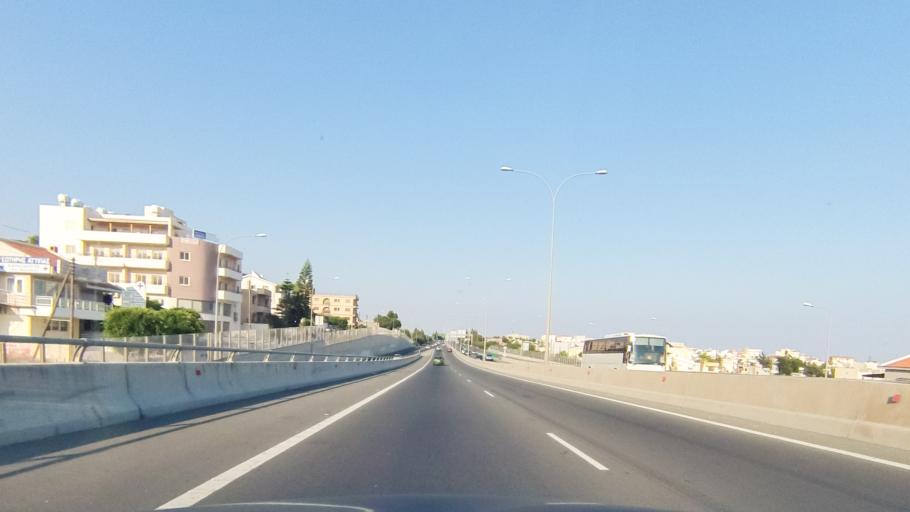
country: CY
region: Limassol
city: Limassol
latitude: 34.7049
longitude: 33.0297
